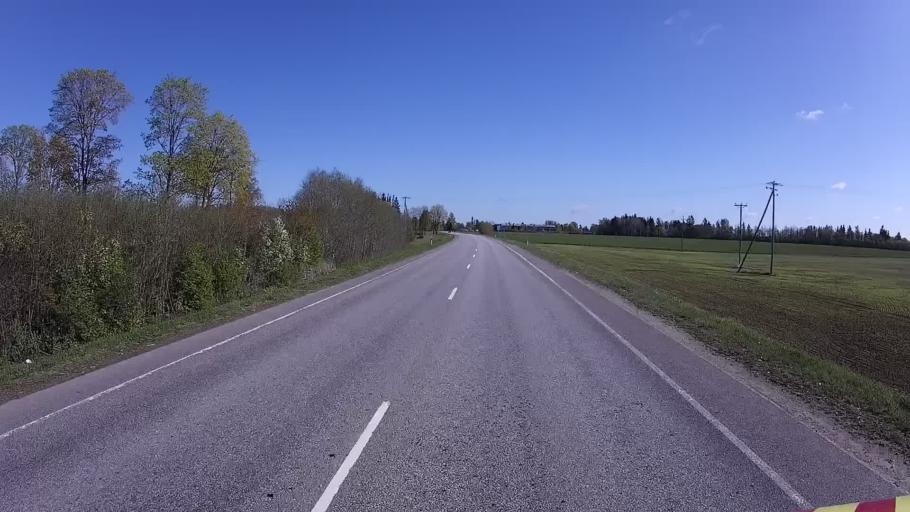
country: EE
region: Jogevamaa
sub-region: Poltsamaa linn
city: Poltsamaa
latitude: 58.7241
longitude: 25.7632
